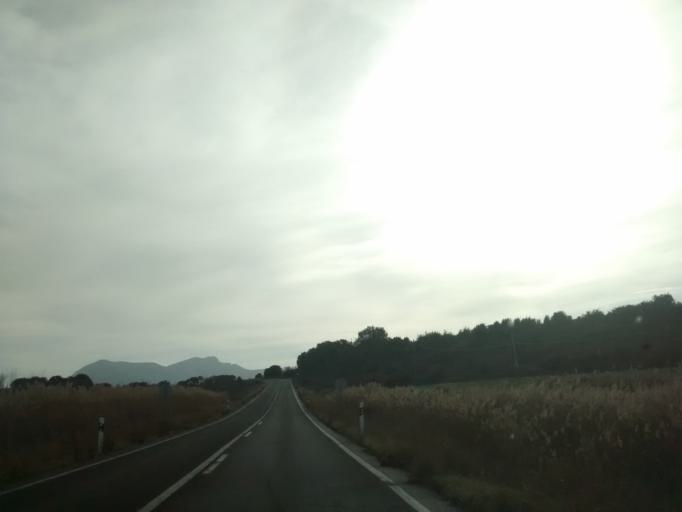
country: ES
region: Aragon
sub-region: Provincia de Huesca
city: Bailo
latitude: 42.5832
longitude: -0.8303
